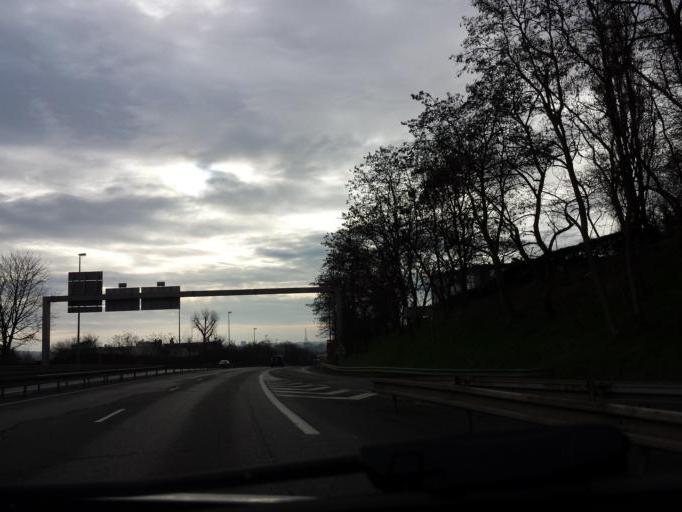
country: FR
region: Ile-de-France
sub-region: Departement du Val-d'Oise
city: Saint-Gratien
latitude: 48.9540
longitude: 2.2765
